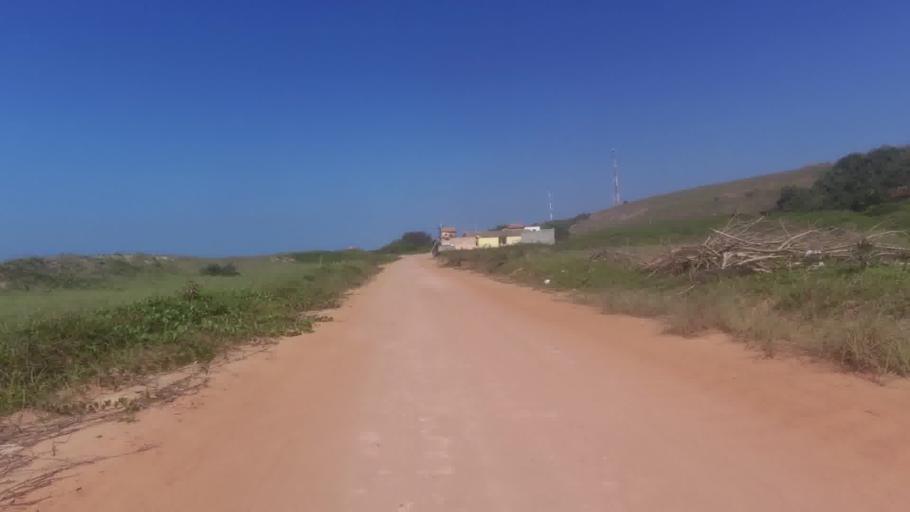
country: BR
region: Espirito Santo
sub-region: Marataizes
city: Marataizes
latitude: -21.0989
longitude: -40.8477
